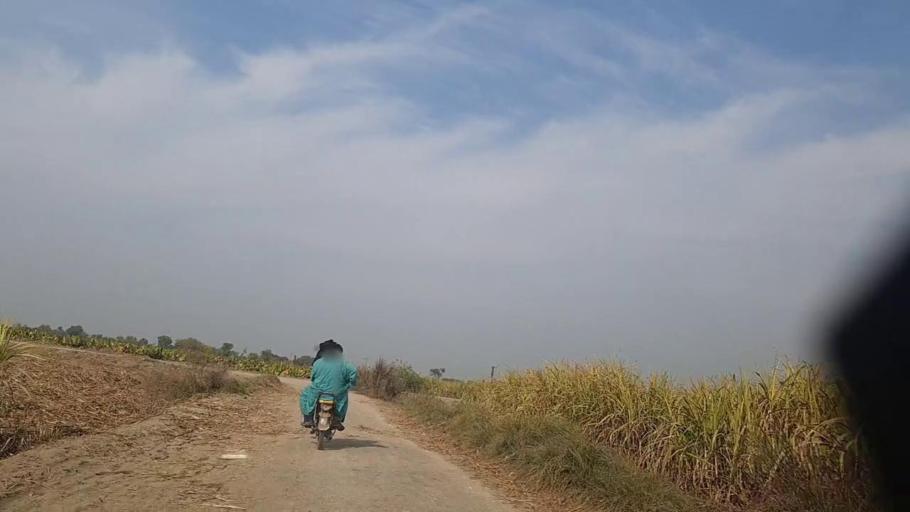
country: PK
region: Sindh
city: Daur
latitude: 26.4041
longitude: 68.2364
